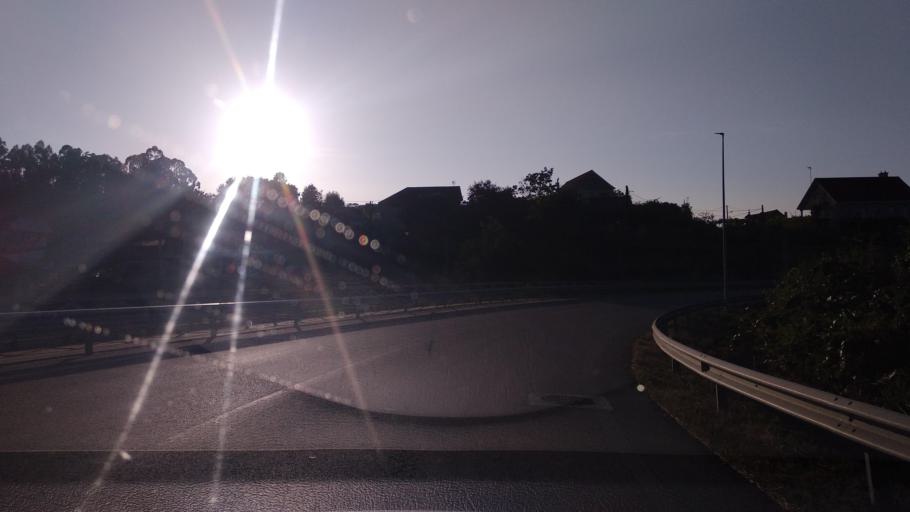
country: ES
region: Galicia
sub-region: Provincia de Pontevedra
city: Redondela
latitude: 42.3347
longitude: -8.5750
